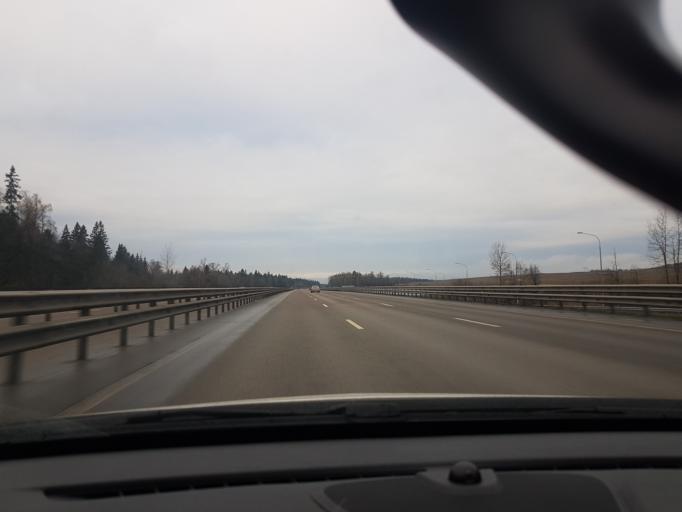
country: RU
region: Moskovskaya
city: Kostrovo
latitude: 55.8663
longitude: 36.7173
